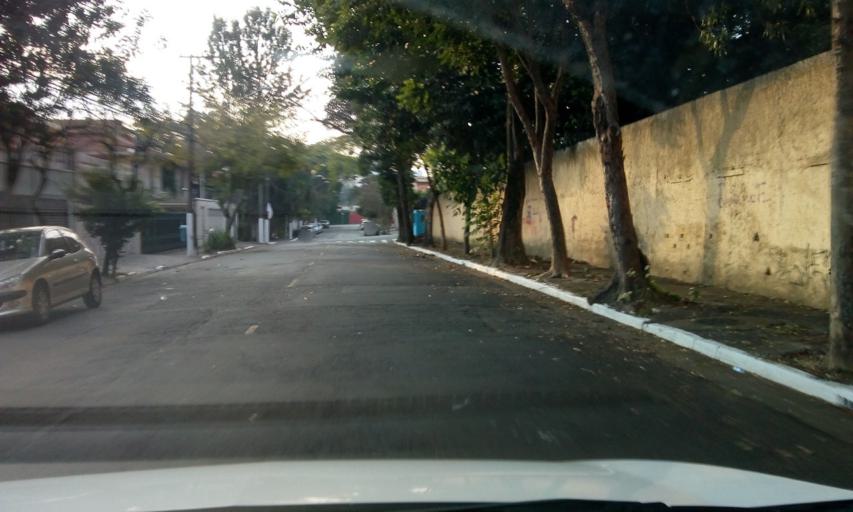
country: BR
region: Sao Paulo
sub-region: Sao Paulo
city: Sao Paulo
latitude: -23.6127
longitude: -46.6519
